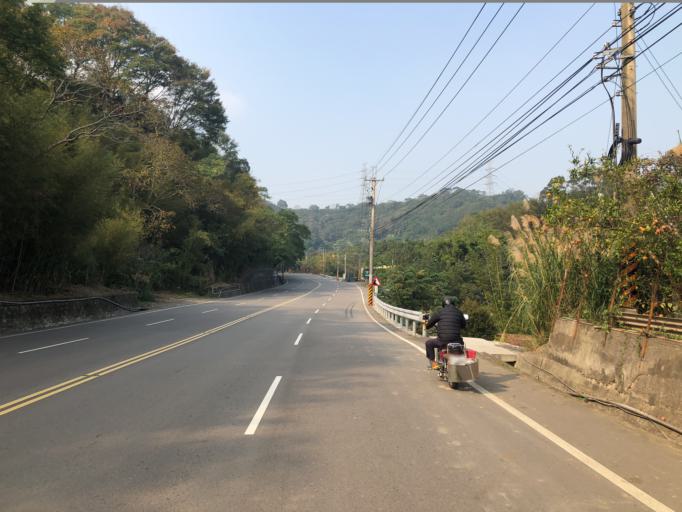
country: TW
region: Taiwan
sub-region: Miaoli
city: Miaoli
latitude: 24.6115
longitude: 120.9586
